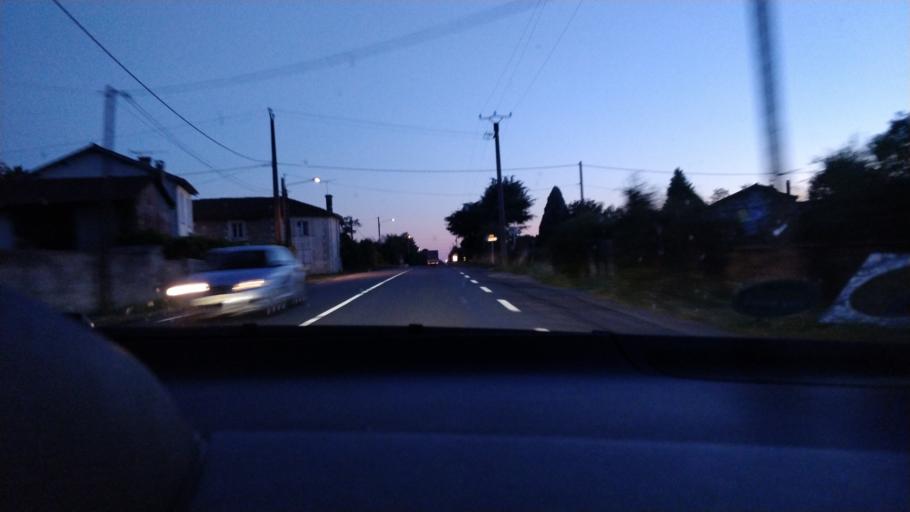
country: FR
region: Poitou-Charentes
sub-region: Departement de la Charente
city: Saint-Claud
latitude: 45.8520
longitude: 0.5051
